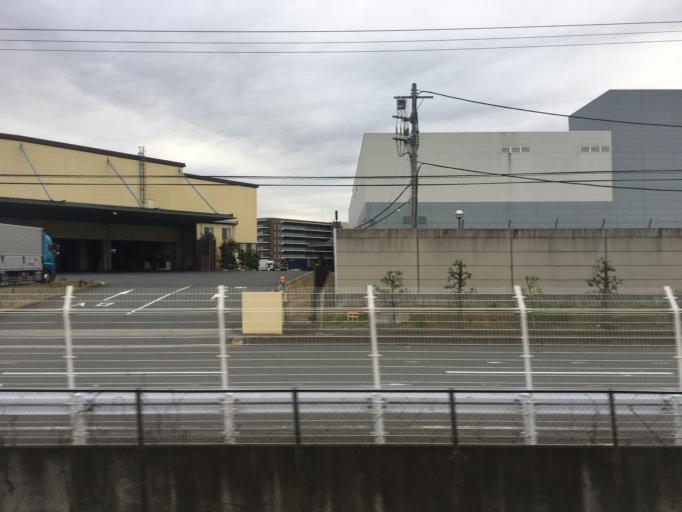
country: JP
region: Chiba
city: Nagareyama
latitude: 35.8552
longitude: 139.8732
